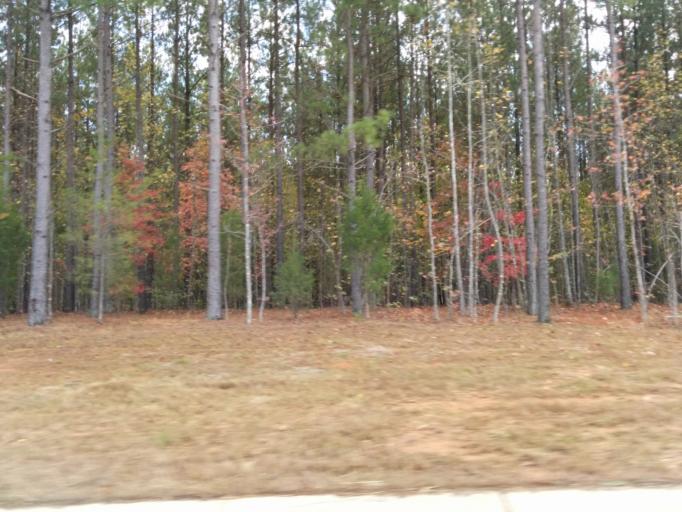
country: US
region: North Carolina
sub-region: Iredell County
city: Troutman
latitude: 35.6438
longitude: -80.8909
